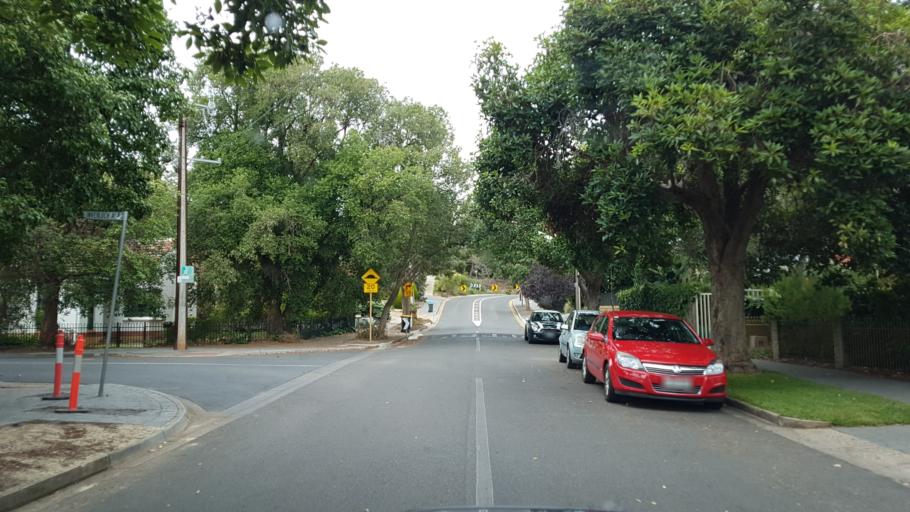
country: AU
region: South Australia
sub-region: Mitcham
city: Mitcham
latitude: -34.9798
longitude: 138.6142
